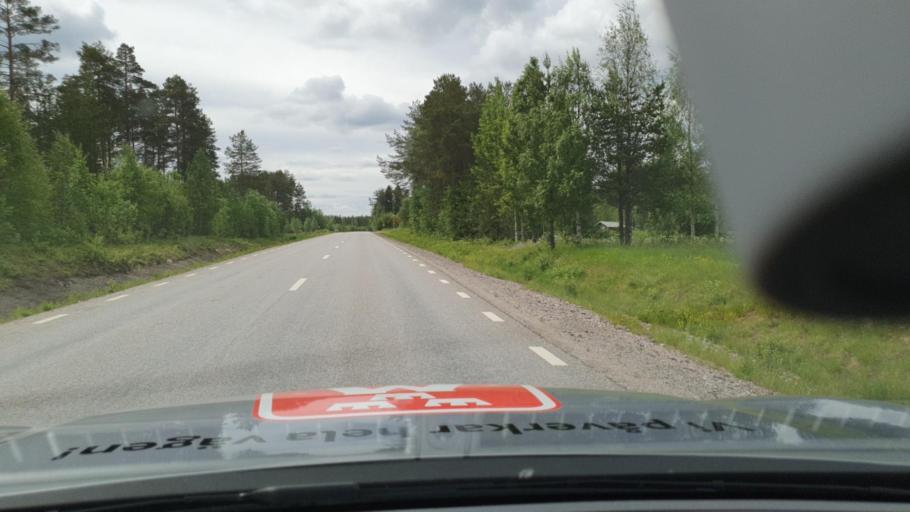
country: SE
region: Norrbotten
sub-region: Kalix Kommun
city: Kalix
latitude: 65.9916
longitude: 23.4787
